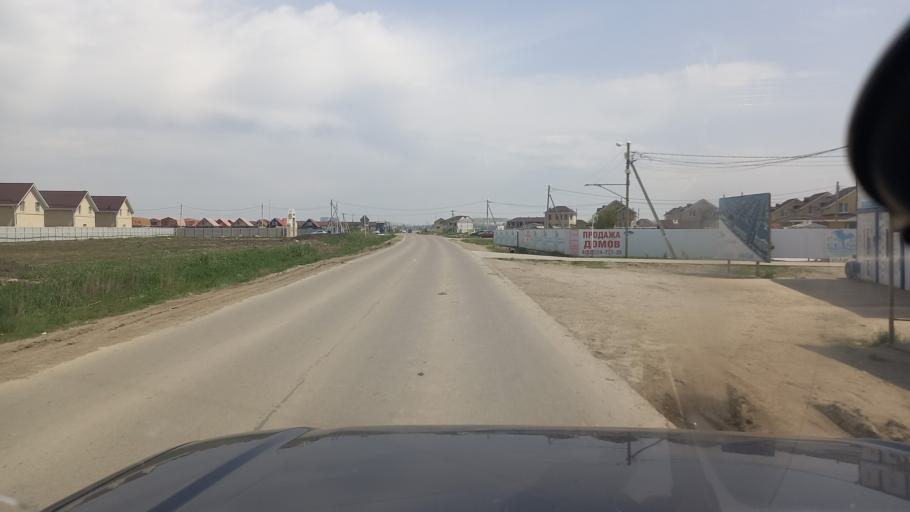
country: RU
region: Adygeya
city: Yablonovskiy
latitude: 44.9854
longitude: 38.9745
